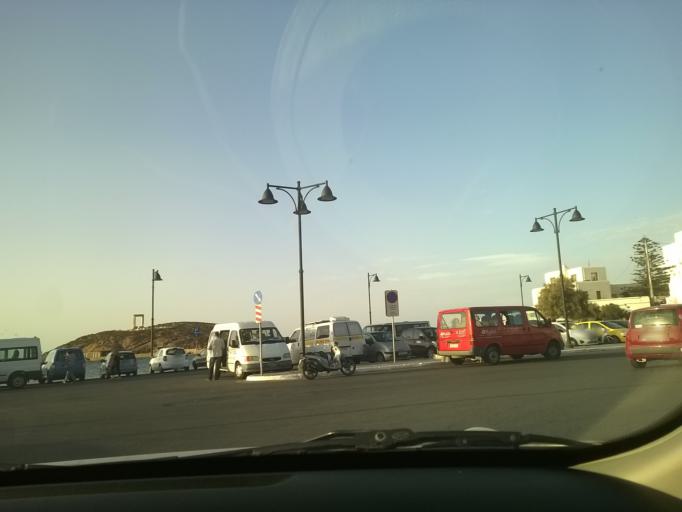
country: GR
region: South Aegean
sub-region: Nomos Kykladon
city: Naxos
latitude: 37.1073
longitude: 25.3740
